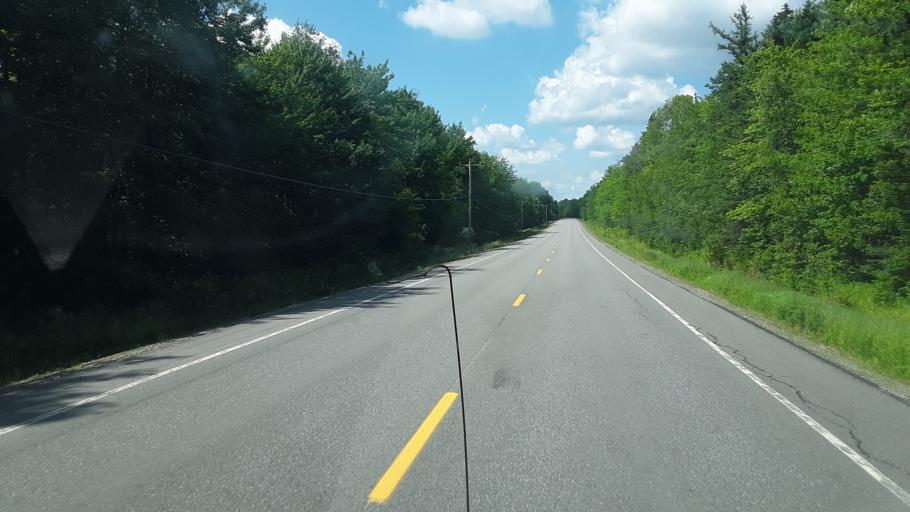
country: US
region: Maine
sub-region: Washington County
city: Machias
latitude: 45.0067
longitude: -67.5535
